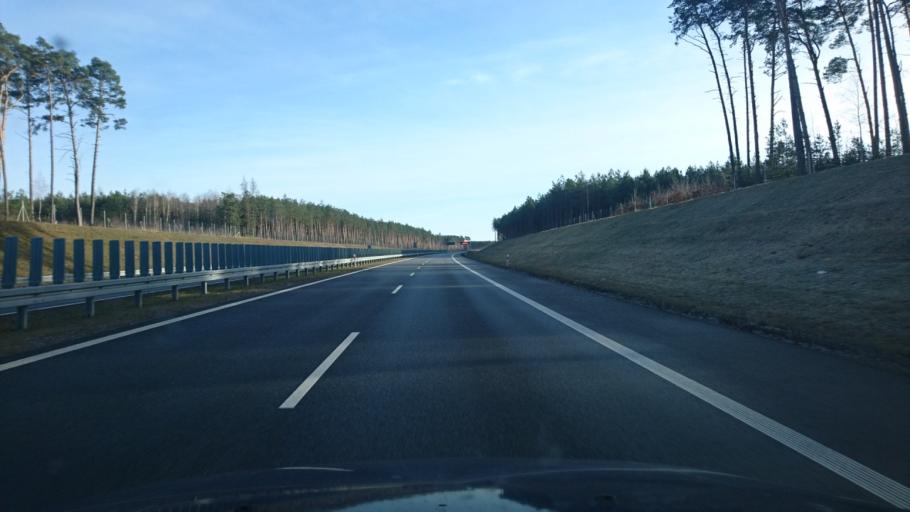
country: PL
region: Greater Poland Voivodeship
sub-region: Powiat kepinski
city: Kepno
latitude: 51.3297
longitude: 17.9755
